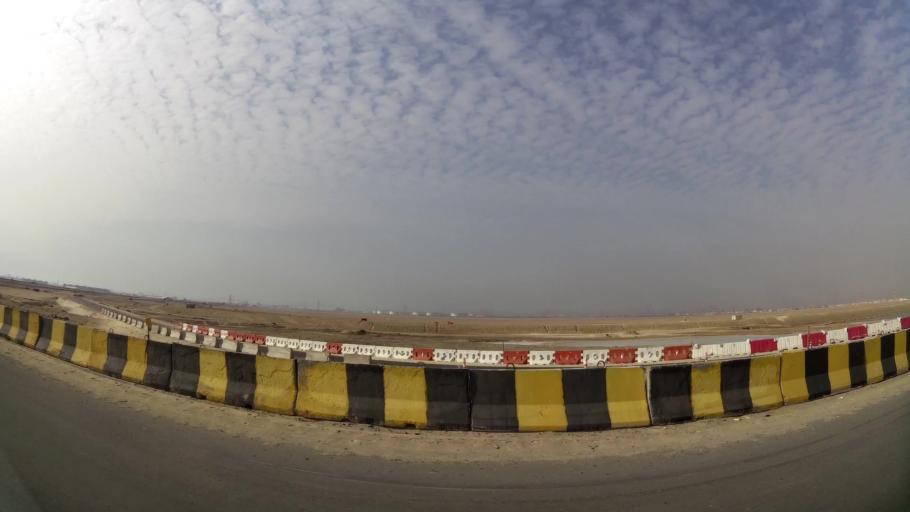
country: AE
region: Abu Dhabi
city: Abu Dhabi
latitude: 24.2787
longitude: 54.5250
